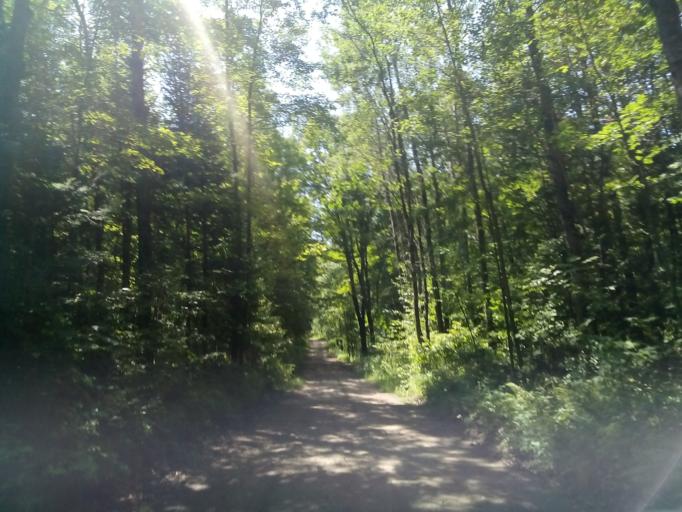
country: US
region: Wisconsin
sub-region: Forest County
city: Crandon
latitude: 45.3622
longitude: -88.5217
